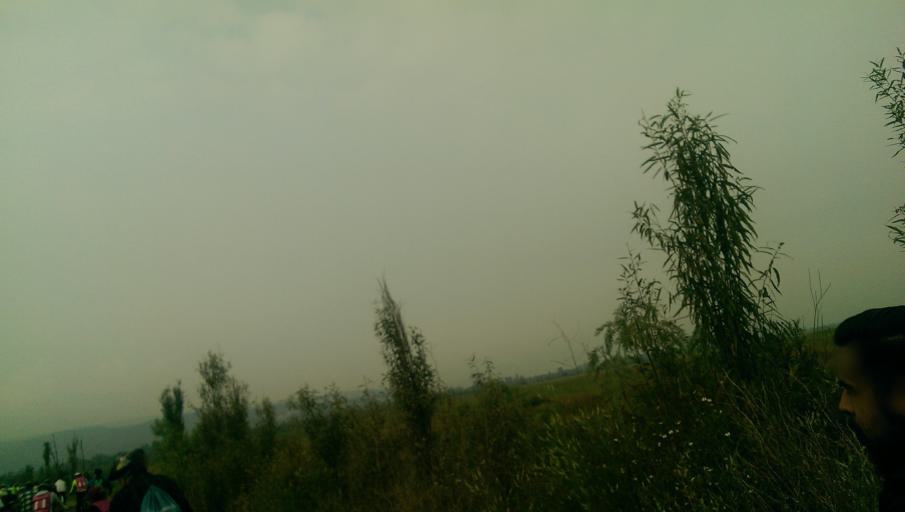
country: MX
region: Mexico City
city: Tlahuac
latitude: 19.2681
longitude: -99.0450
